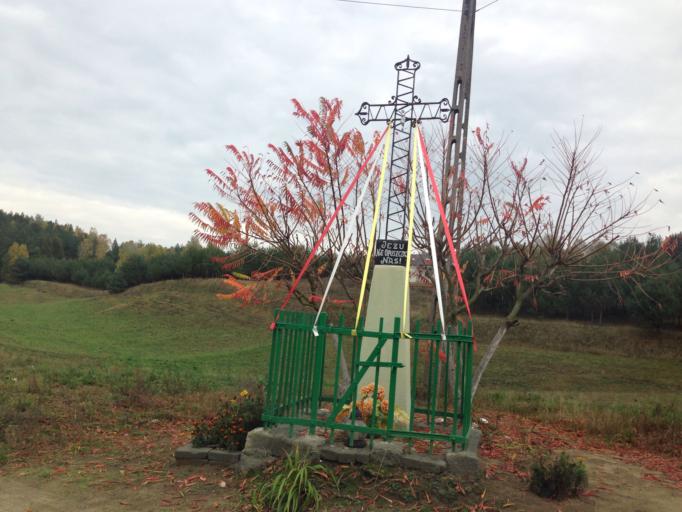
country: PL
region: Kujawsko-Pomorskie
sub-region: Powiat brodnicki
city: Bartniczka
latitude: 53.2713
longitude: 19.6731
